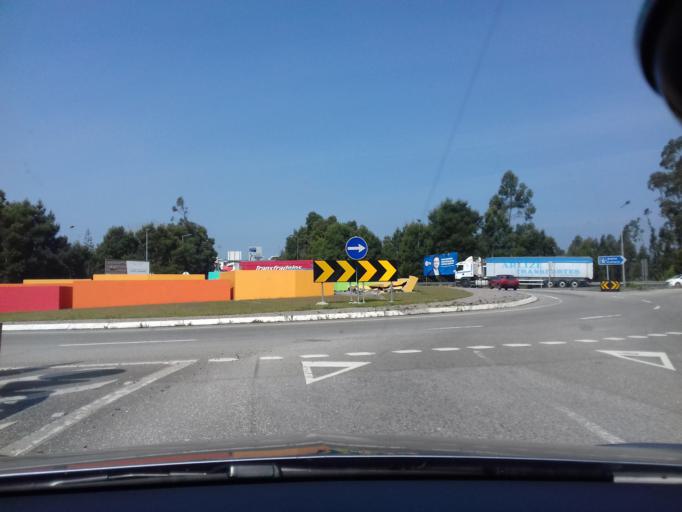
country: PT
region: Aveiro
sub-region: Espinho
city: Silvalde
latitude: 41.0085
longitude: -8.6204
